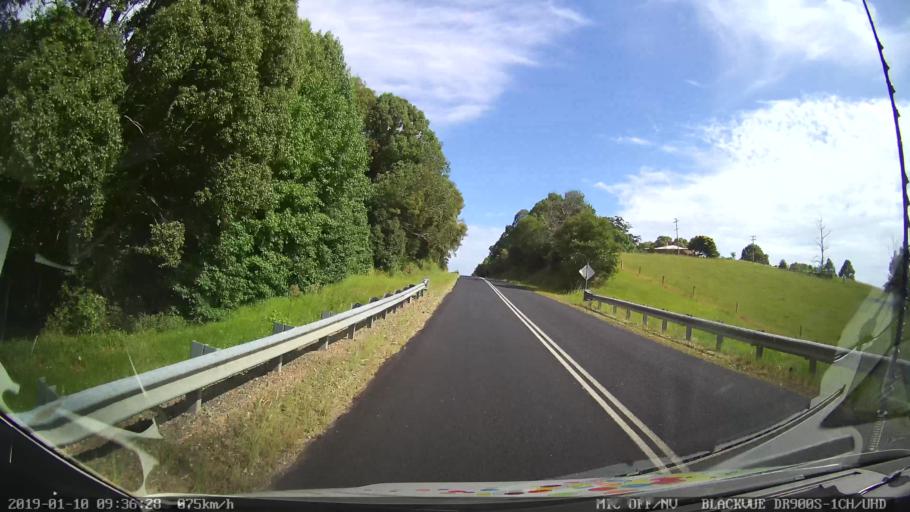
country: AU
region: New South Wales
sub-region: Coffs Harbour
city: Nana Glen
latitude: -30.1984
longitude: 153.0142
